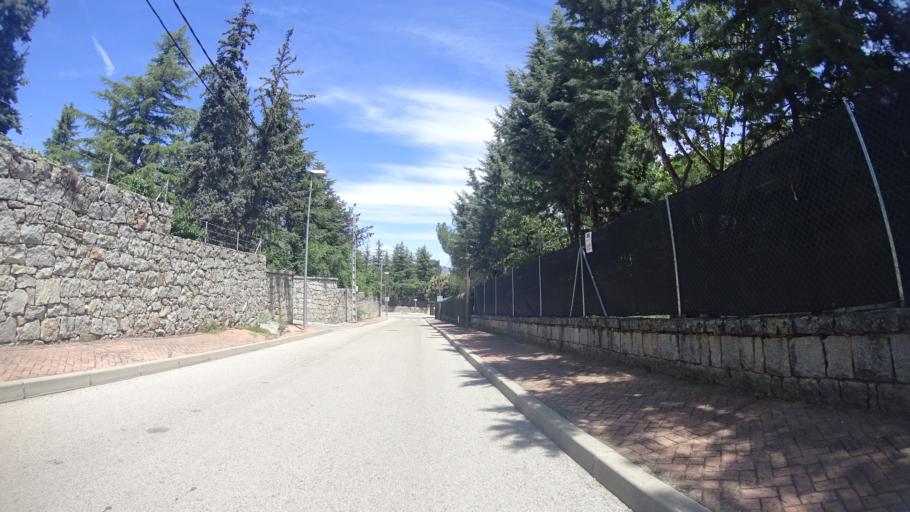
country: ES
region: Madrid
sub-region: Provincia de Madrid
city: Galapagar
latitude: 40.5755
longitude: -3.9932
